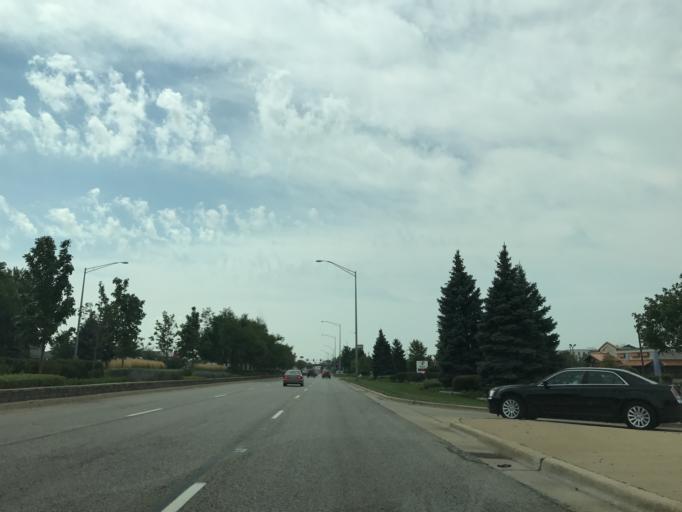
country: US
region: Illinois
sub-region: Will County
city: Bolingbrook
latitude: 41.6907
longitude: -88.0682
